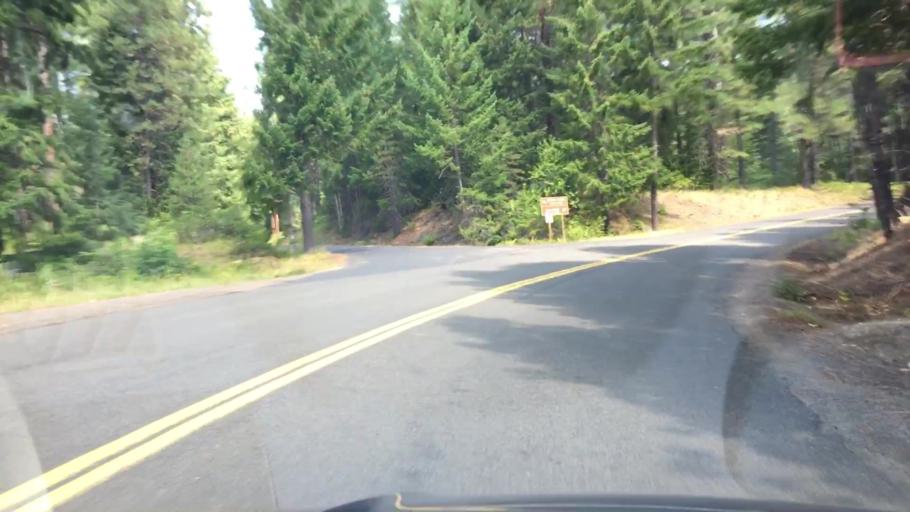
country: US
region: Washington
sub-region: Klickitat County
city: White Salmon
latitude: 46.0232
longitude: -121.5264
